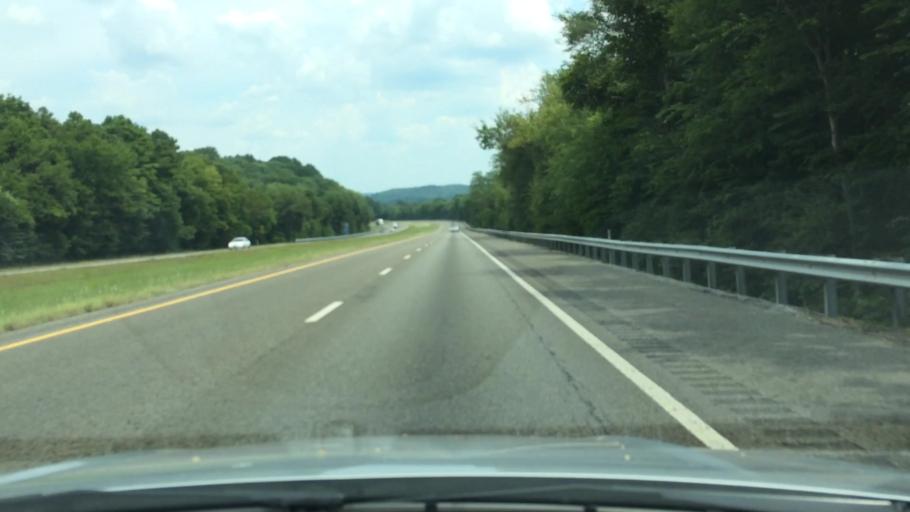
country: US
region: Tennessee
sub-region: Marshall County
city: Cornersville
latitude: 35.4094
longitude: -86.8787
